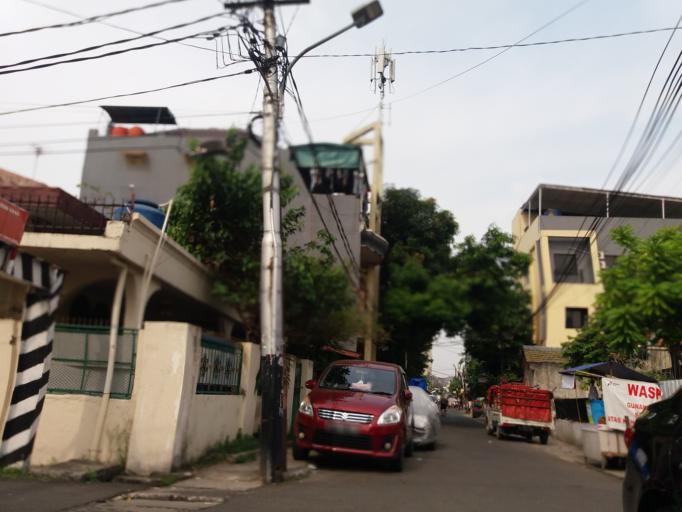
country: ID
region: Jakarta Raya
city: Jakarta
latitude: -6.1848
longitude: 106.8273
